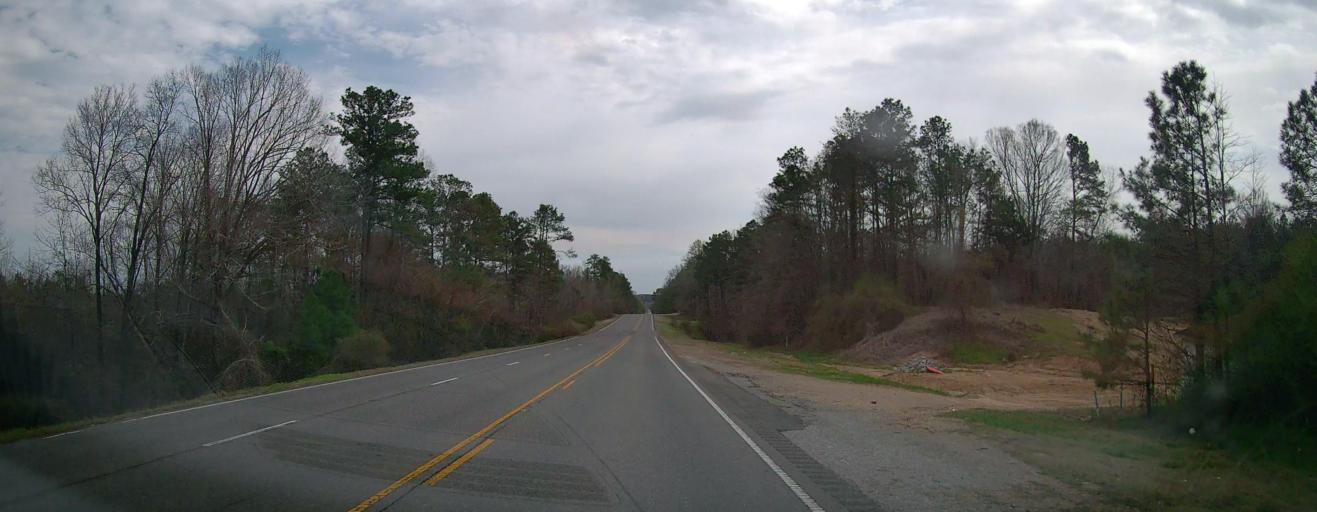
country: US
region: Alabama
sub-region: Marion County
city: Guin
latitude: 34.0258
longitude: -87.9406
